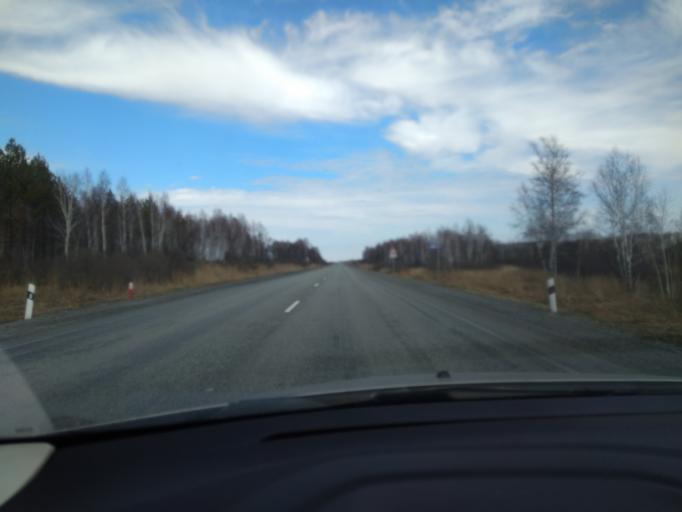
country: RU
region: Sverdlovsk
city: Pyshma
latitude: 57.0063
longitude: 63.3334
